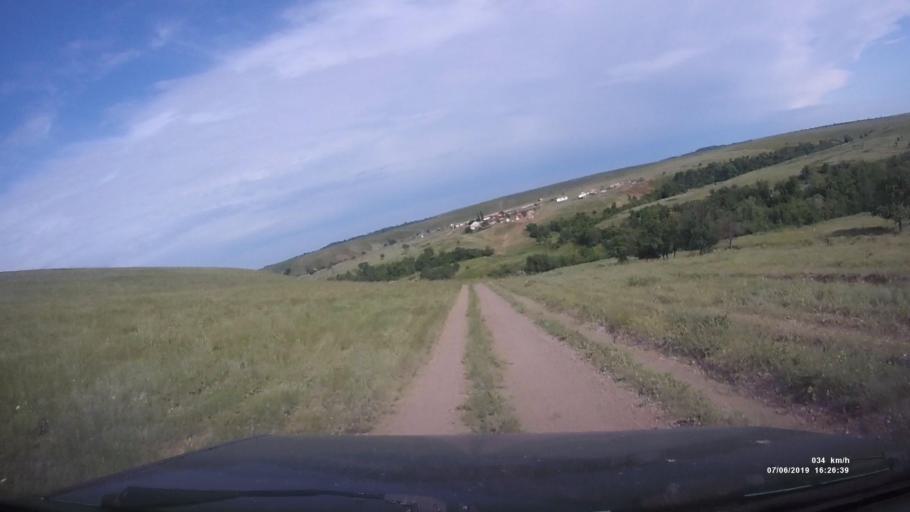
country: RU
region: Rostov
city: Kamensk-Shakhtinskiy
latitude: 48.2524
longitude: 40.3136
